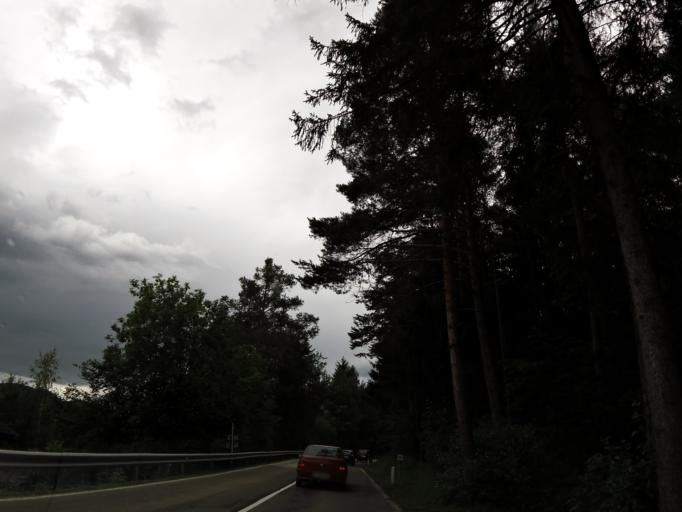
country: IT
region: Trentino-Alto Adige
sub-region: Bolzano
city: Siusi
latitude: 46.5332
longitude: 11.5399
